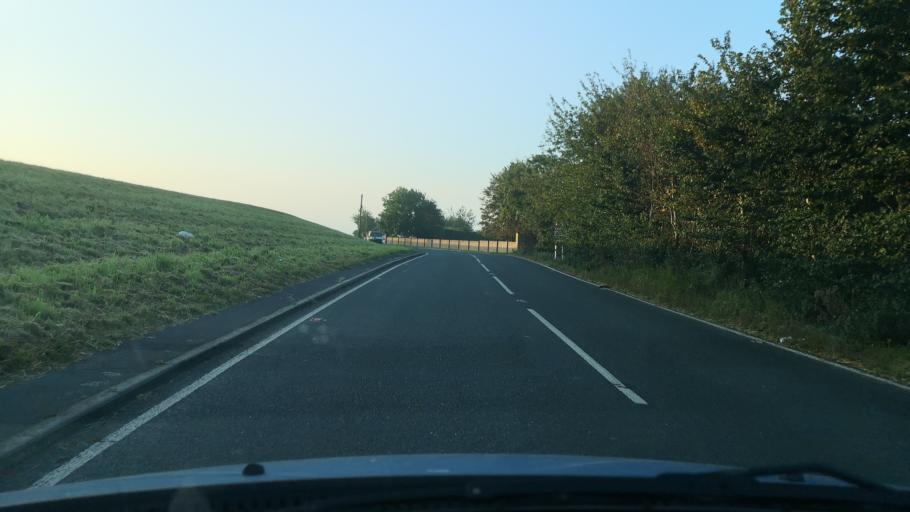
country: GB
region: England
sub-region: East Riding of Yorkshire
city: Goole
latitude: 53.6867
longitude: -0.8605
